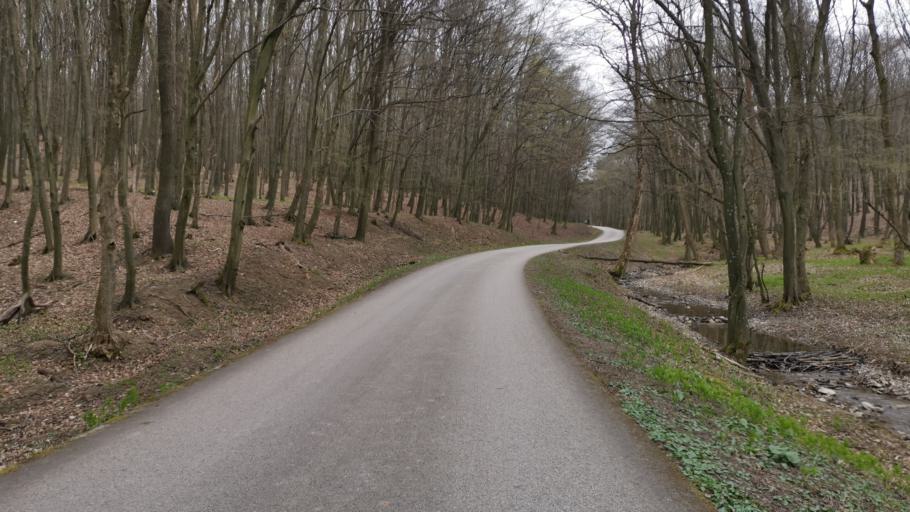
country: CZ
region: South Moravian
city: Sudomerice
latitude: 48.8189
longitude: 17.3044
